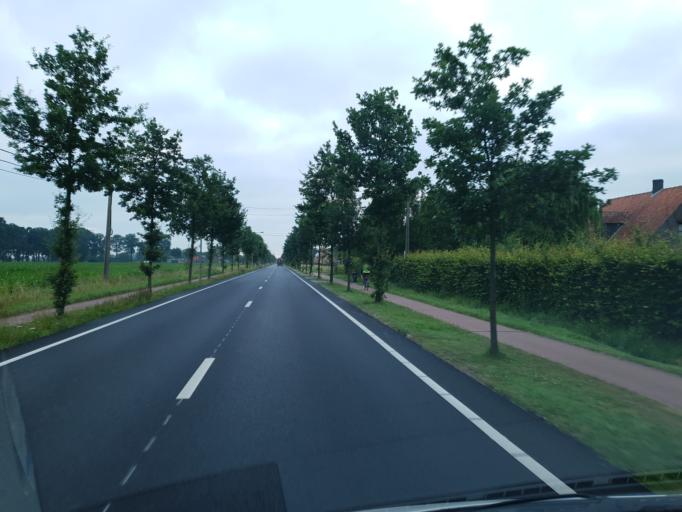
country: BE
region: Flanders
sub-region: Provincie Antwerpen
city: Rijkevorsel
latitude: 51.3673
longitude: 4.7086
